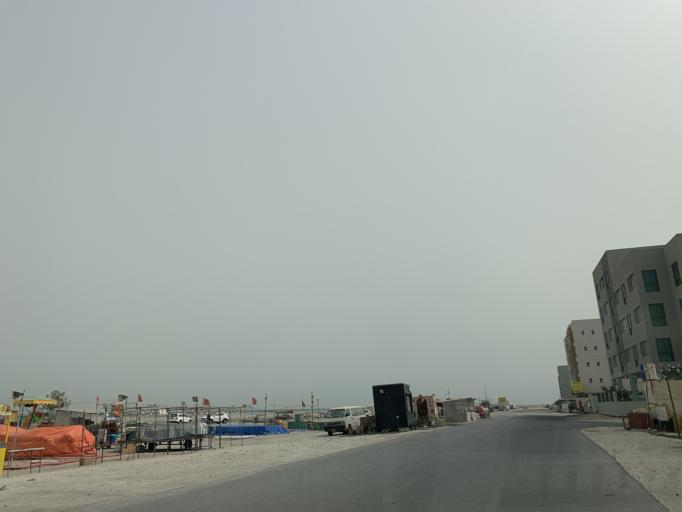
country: BH
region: Manama
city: Jidd Hafs
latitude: 26.2382
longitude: 50.5245
